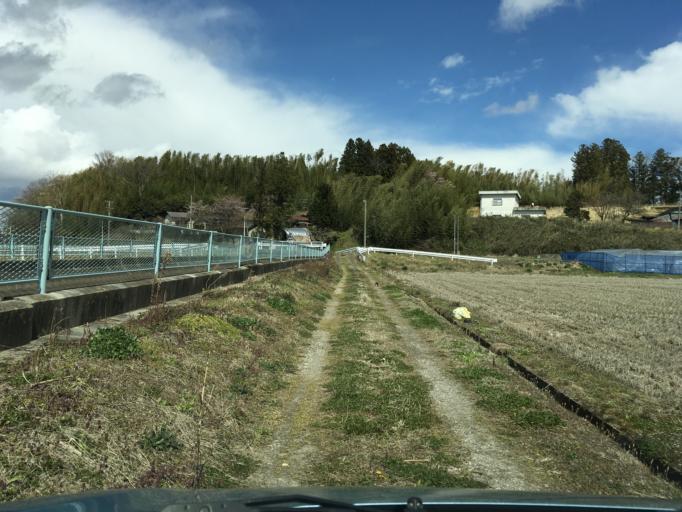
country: JP
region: Miyagi
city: Wakuya
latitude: 38.7063
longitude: 141.1562
